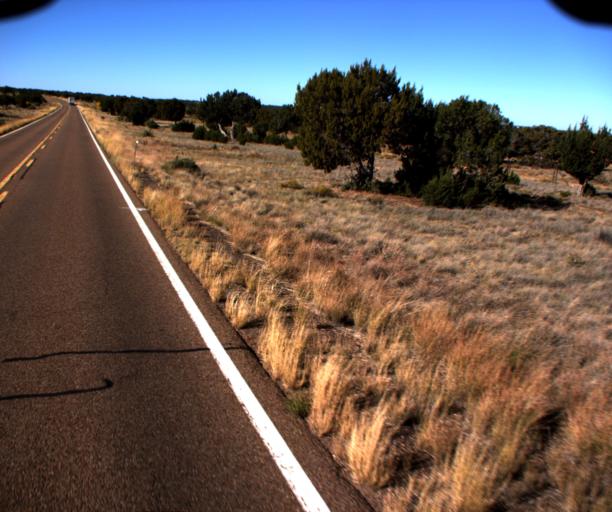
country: US
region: Arizona
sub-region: Navajo County
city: Heber-Overgaard
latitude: 34.5088
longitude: -110.4467
